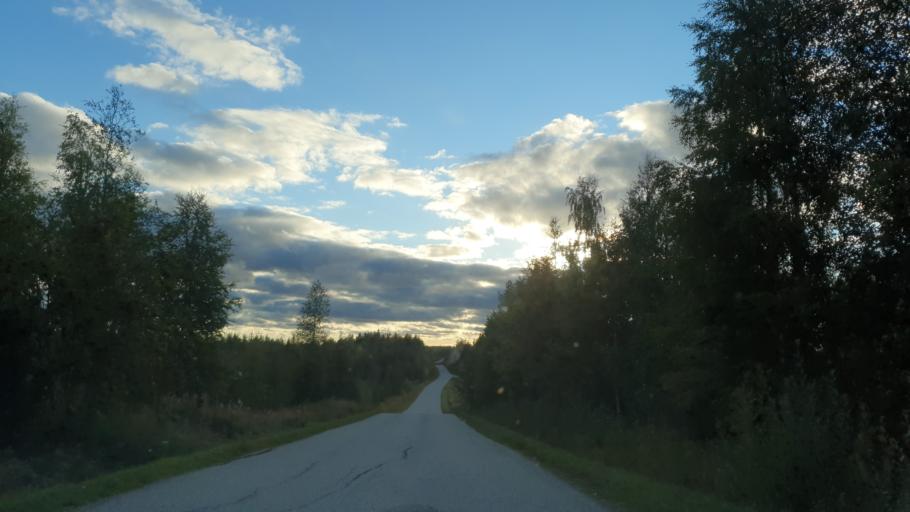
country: FI
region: Kainuu
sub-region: Kehys-Kainuu
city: Kuhmo
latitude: 63.9515
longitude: 29.7981
